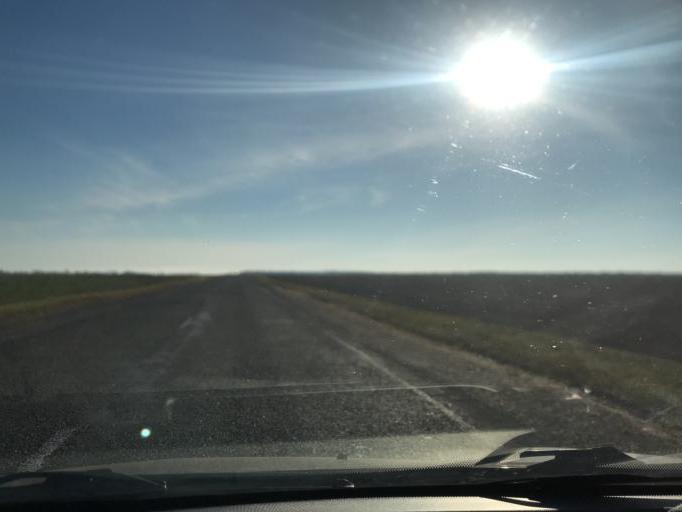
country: BY
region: Gomel
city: Brahin
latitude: 51.7909
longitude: 30.1763
